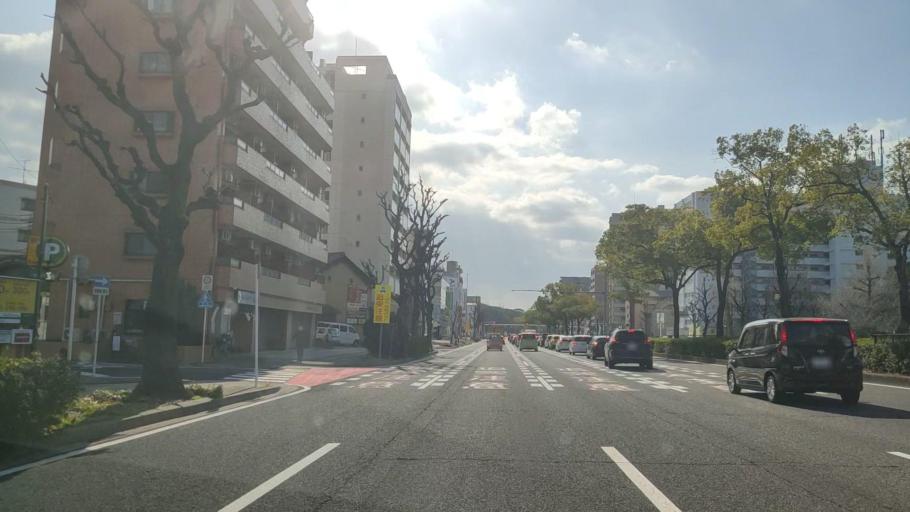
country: JP
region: Aichi
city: Nagoya-shi
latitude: 35.1318
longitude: 136.9040
